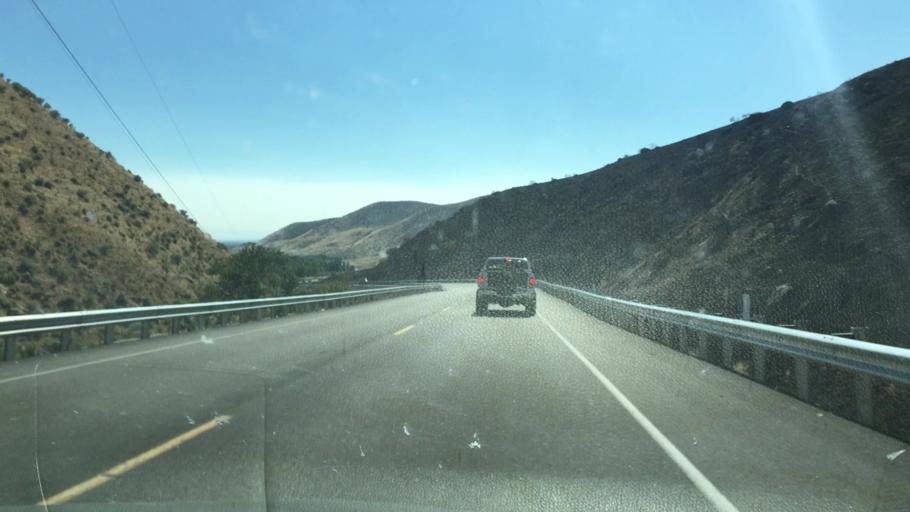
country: US
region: Idaho
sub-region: Ada County
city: Eagle
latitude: 43.7580
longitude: -116.2771
